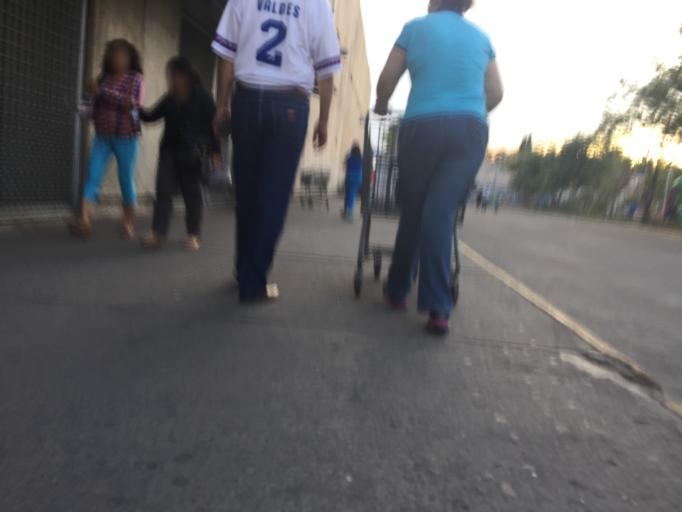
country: MX
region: Mexico City
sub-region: Iztacalco
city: Iztacalco
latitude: 19.3852
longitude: -99.0801
